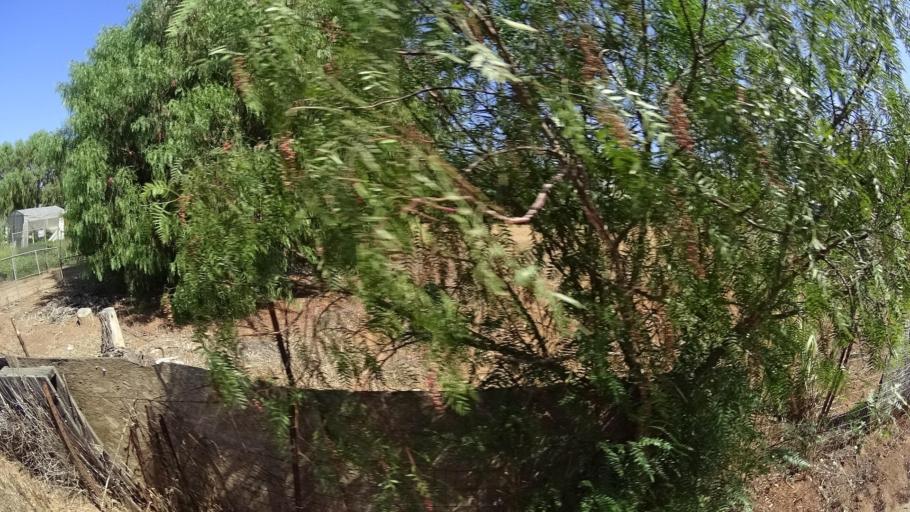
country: US
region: California
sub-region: San Diego County
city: Escondido
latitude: 33.0939
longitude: -117.0902
